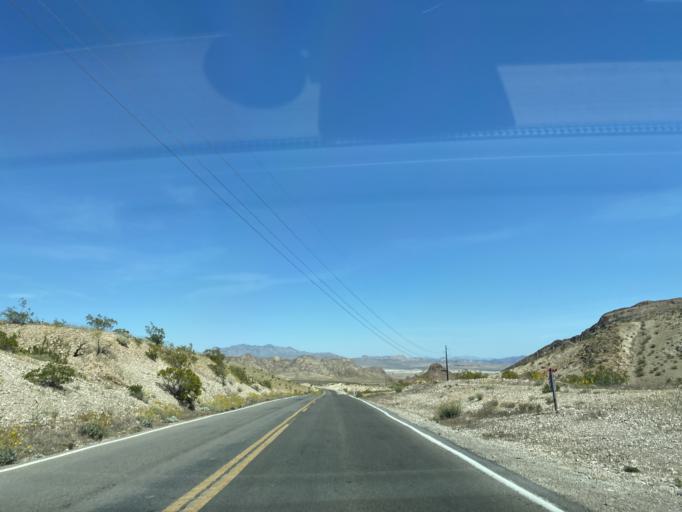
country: US
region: Nevada
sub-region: Clark County
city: Nellis Air Force Base
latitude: 36.2015
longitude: -114.9786
